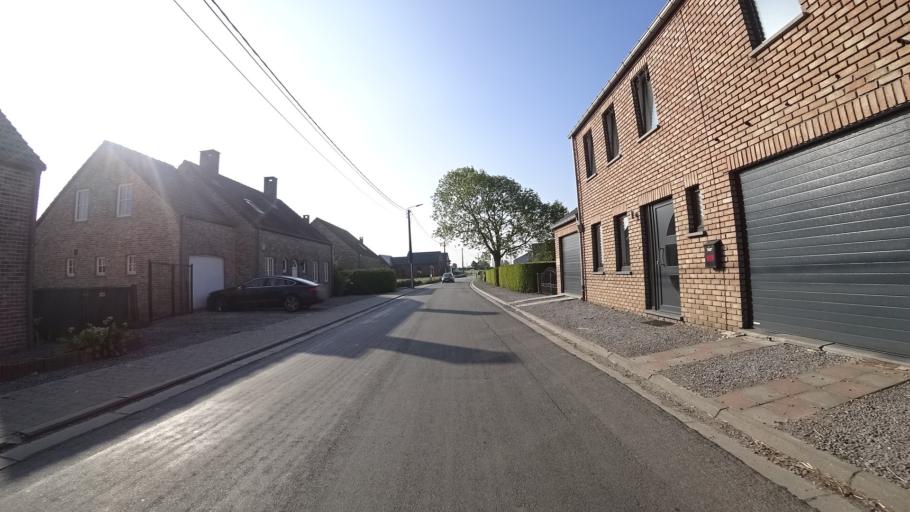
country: BE
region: Wallonia
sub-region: Province du Brabant Wallon
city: Perwez
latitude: 50.5493
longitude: 4.8049
